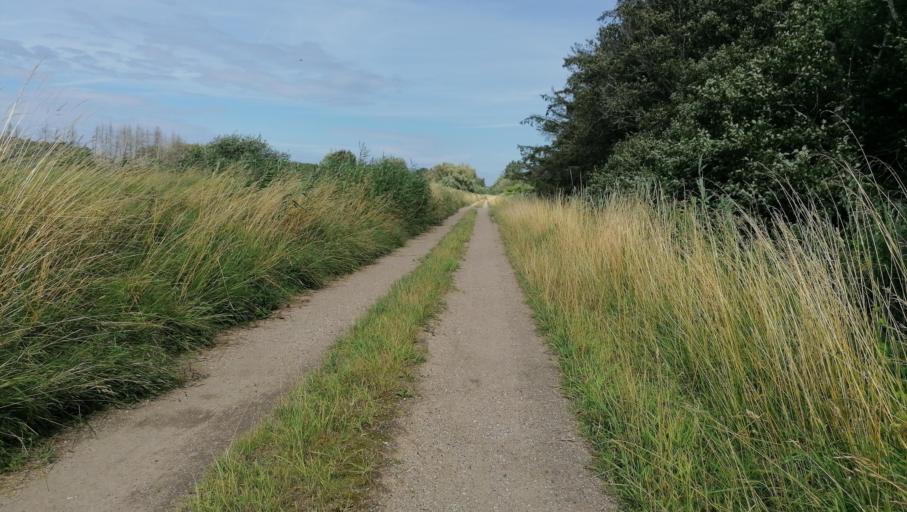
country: DK
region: Zealand
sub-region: Odsherred Kommune
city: Horve
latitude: 55.7822
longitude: 11.4189
